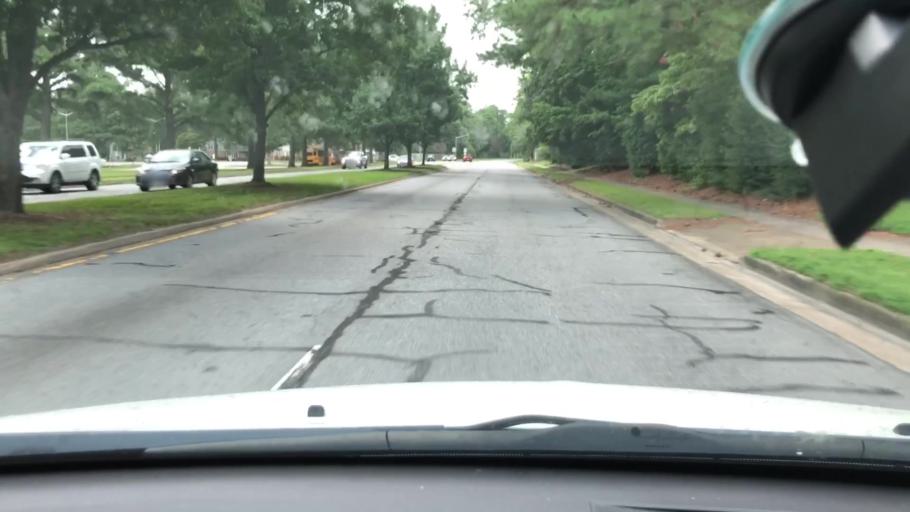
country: US
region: Virginia
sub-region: City of Chesapeake
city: Chesapeake
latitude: 36.8149
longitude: -76.1799
